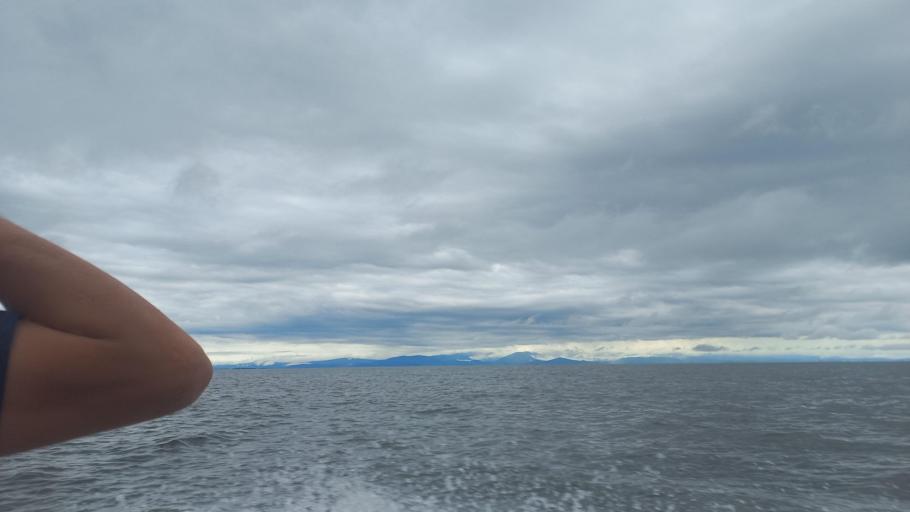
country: CO
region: Antioquia
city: Turbo
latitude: 7.9286
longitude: -76.8110
